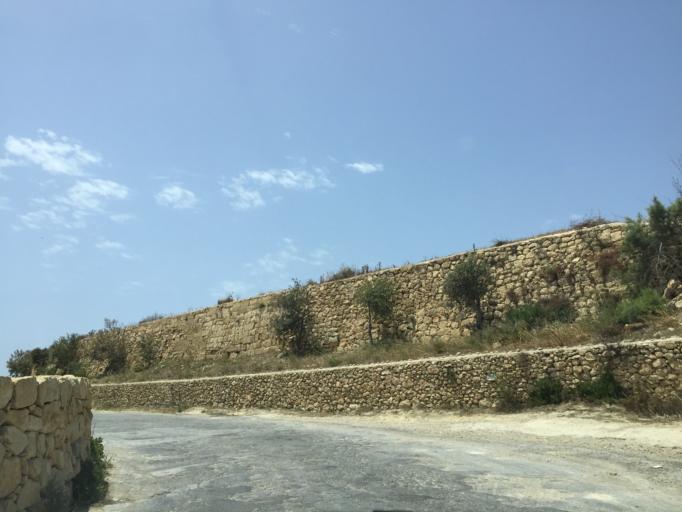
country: MT
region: Saint Lucia
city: Saint Lucia
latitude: 36.0362
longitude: 14.2067
